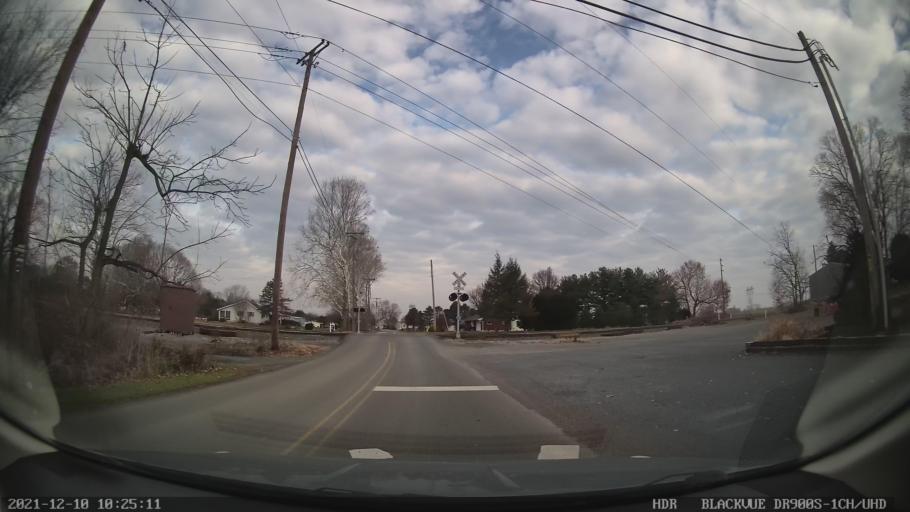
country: US
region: Pennsylvania
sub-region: Berks County
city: Topton
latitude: 40.4876
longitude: -75.7419
